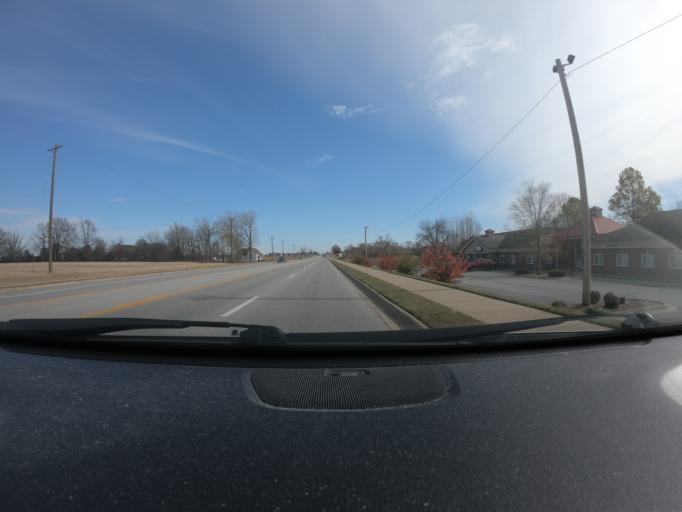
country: US
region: Arkansas
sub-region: Benton County
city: Bentonville
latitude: 36.3358
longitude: -94.2330
